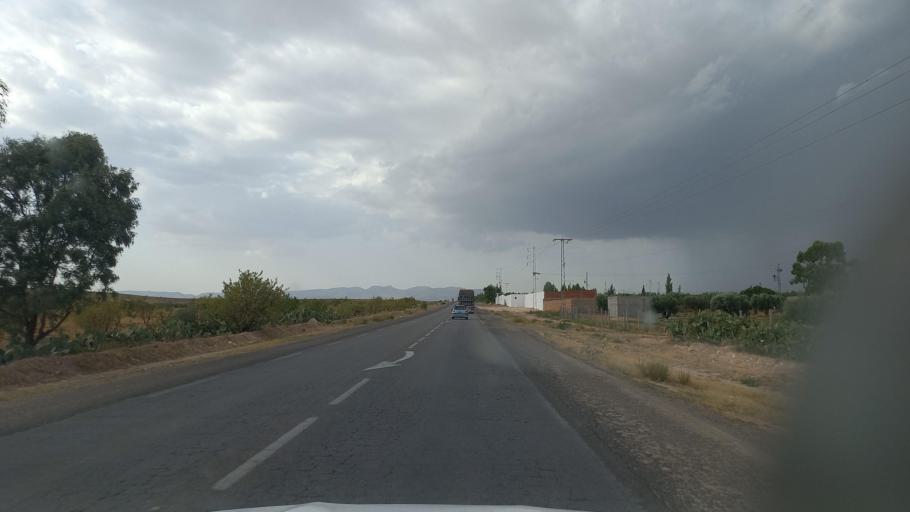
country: TN
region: Al Qasrayn
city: Sbiba
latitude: 35.3101
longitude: 9.0855
